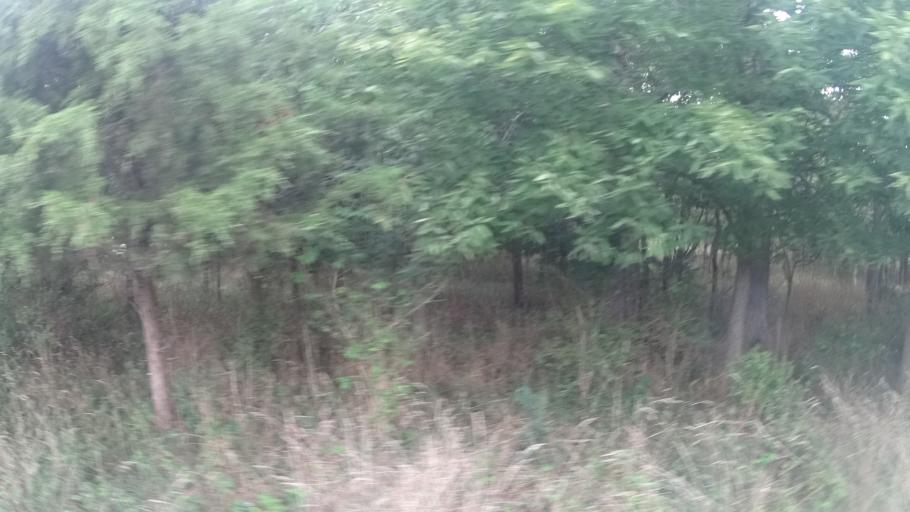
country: US
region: Ohio
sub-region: Erie County
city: Sandusky
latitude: 41.6047
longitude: -82.6867
